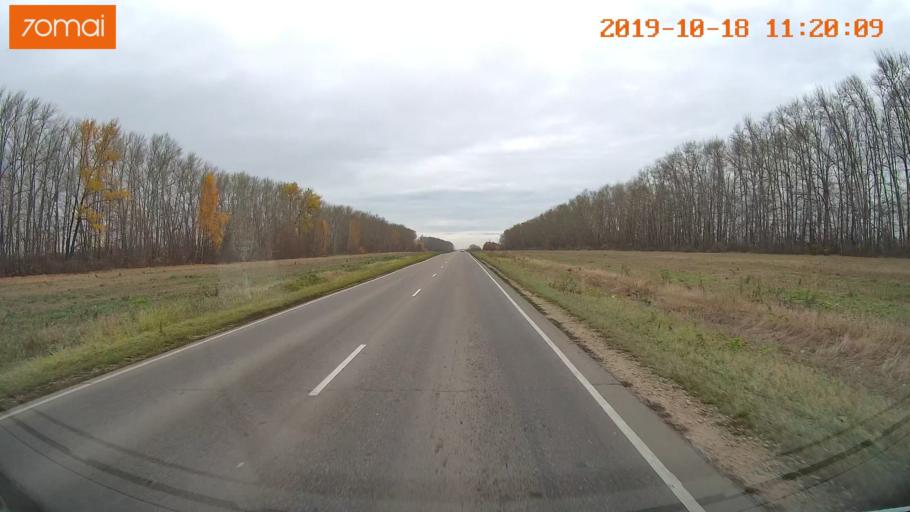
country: RU
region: Tula
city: Kimovsk
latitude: 54.0560
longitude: 38.5572
